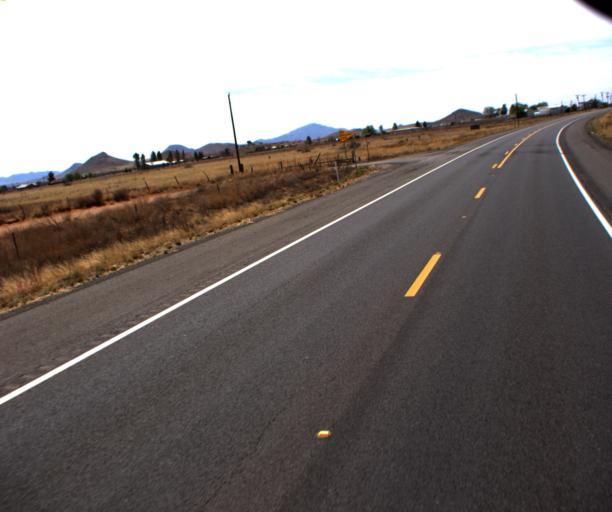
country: US
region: Arizona
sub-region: Cochise County
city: Willcox
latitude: 31.8907
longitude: -109.6955
